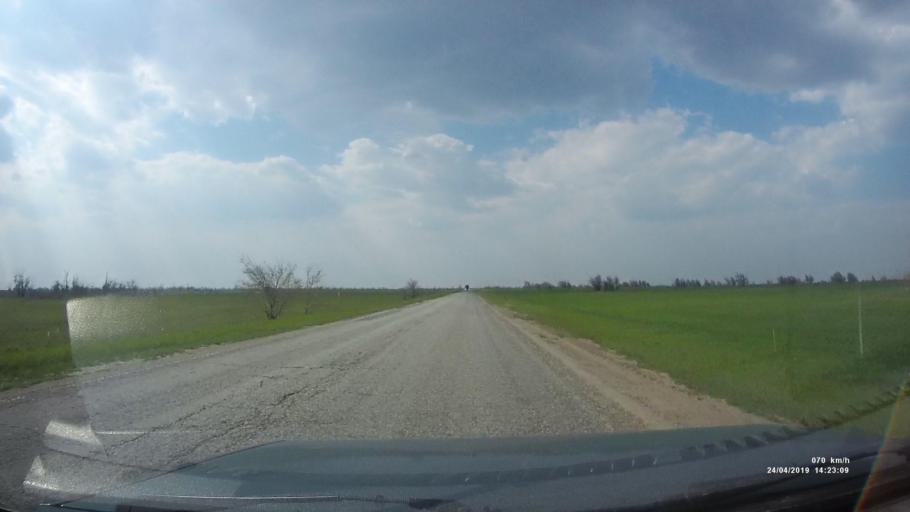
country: RU
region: Kalmykiya
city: Arshan'
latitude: 46.3196
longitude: 44.1182
